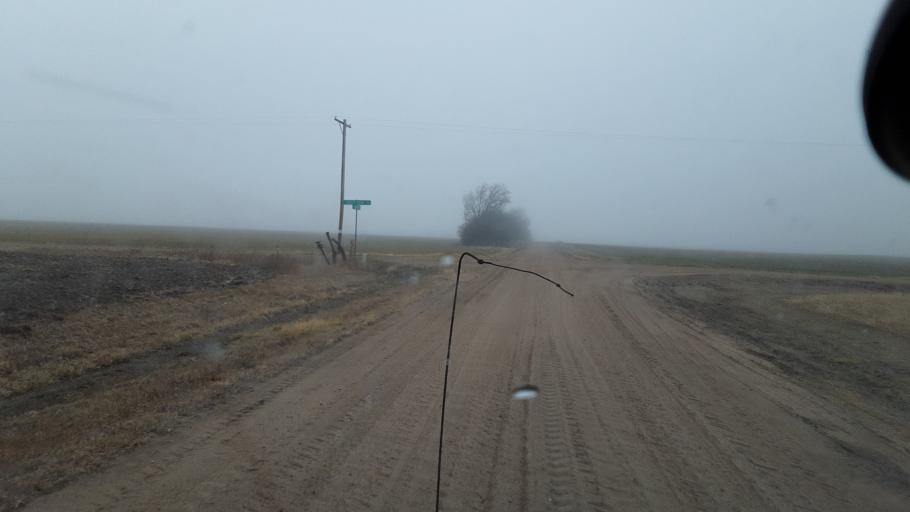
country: US
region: Kansas
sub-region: Reno County
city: South Hutchinson
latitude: 37.9553
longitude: -97.9585
